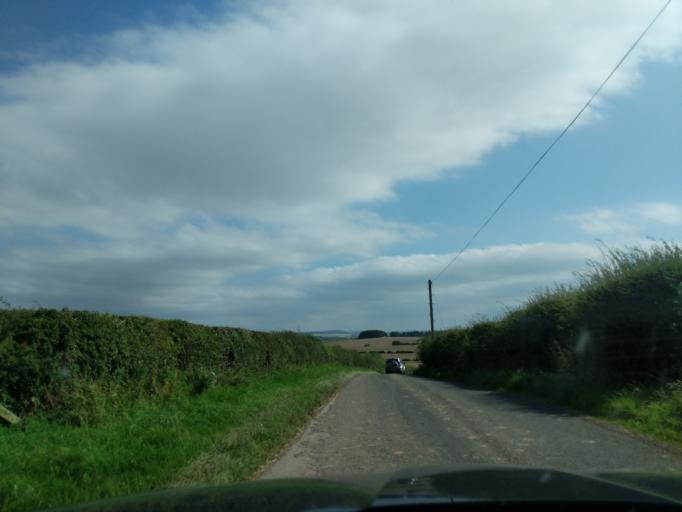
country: GB
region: England
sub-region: Northumberland
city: Ford
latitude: 55.6538
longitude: -2.1471
